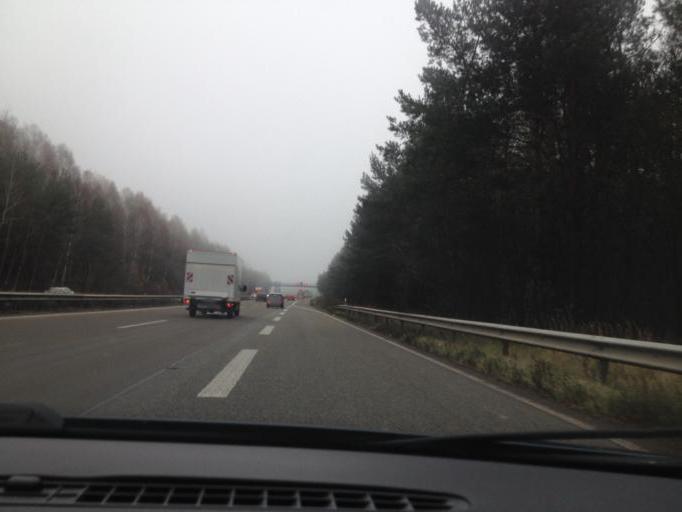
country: DE
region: Rheinland-Pfalz
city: Otterbach
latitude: 49.4488
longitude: 7.7139
